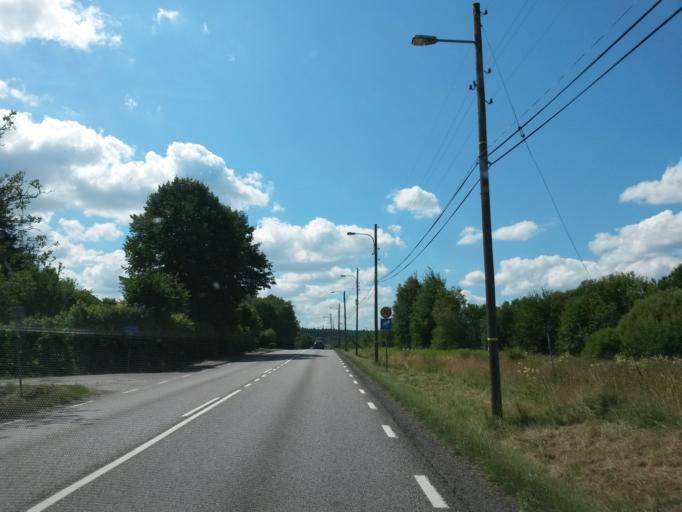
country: SE
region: Vaestra Goetaland
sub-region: Partille Kommun
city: Partille
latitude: 57.7950
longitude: 12.1367
